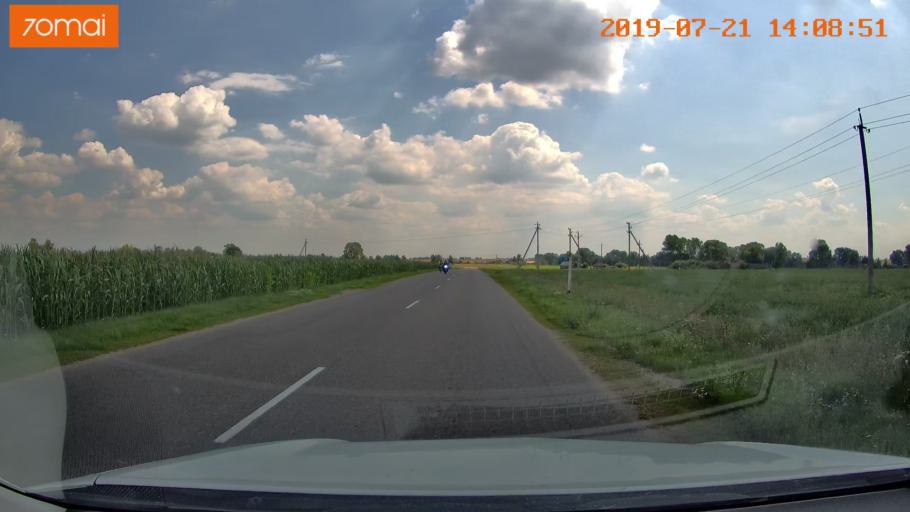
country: BY
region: Grodnenskaya
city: Karelichy
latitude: 53.6700
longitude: 26.1297
